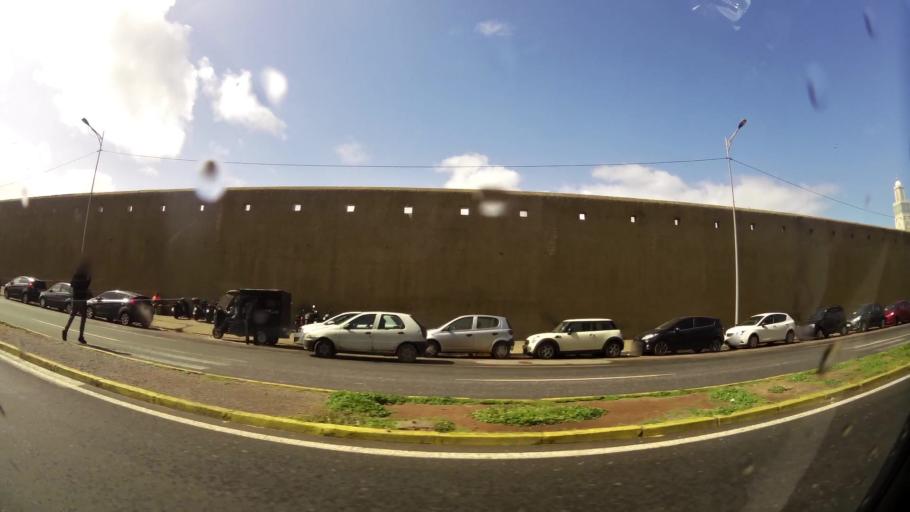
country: MA
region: Grand Casablanca
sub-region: Casablanca
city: Casablanca
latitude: 33.6081
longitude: -7.6248
